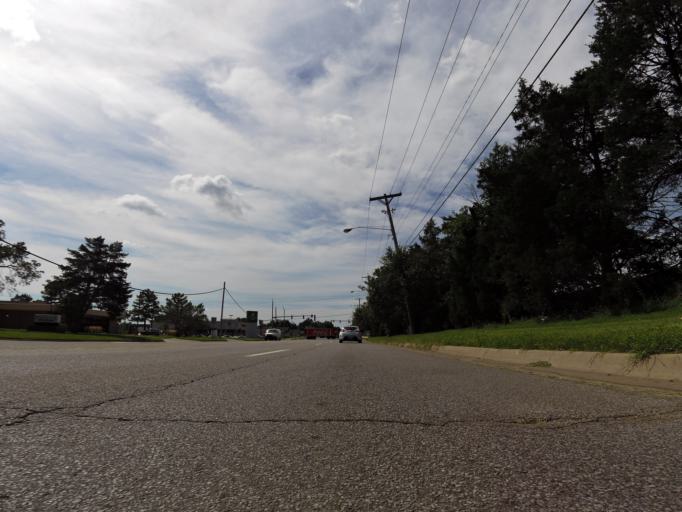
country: US
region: Kansas
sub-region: Sedgwick County
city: Bellaire
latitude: 37.7095
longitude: -97.2624
